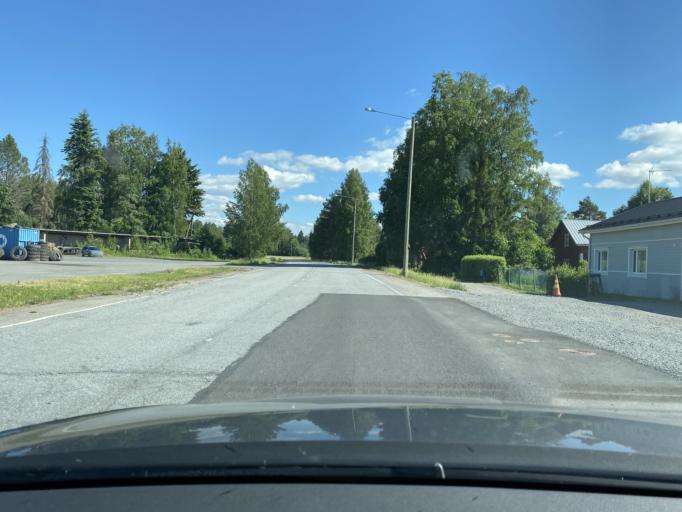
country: FI
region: Satakunta
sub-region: Pori
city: Huittinen
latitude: 61.1775
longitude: 22.7072
